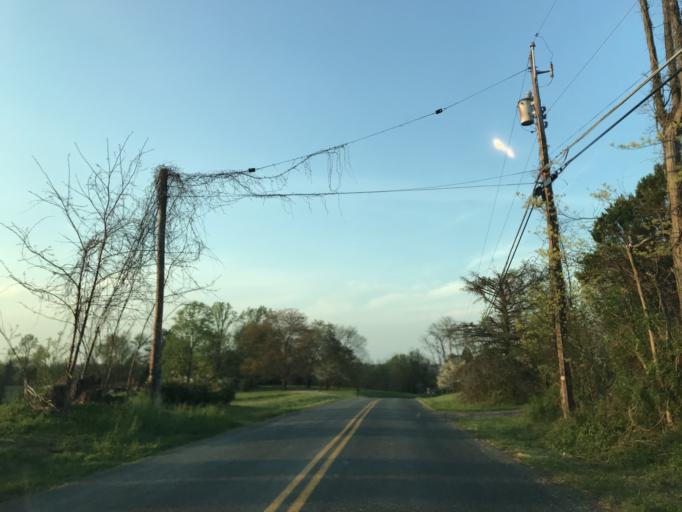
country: US
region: Maryland
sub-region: Harford County
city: Jarrettsville
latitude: 39.6014
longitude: -76.4165
